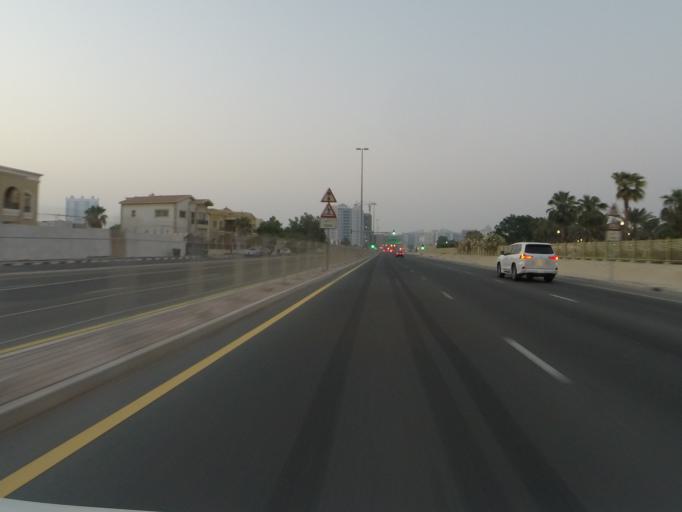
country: AE
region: Dubai
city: Dubai
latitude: 25.1009
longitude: 55.1996
